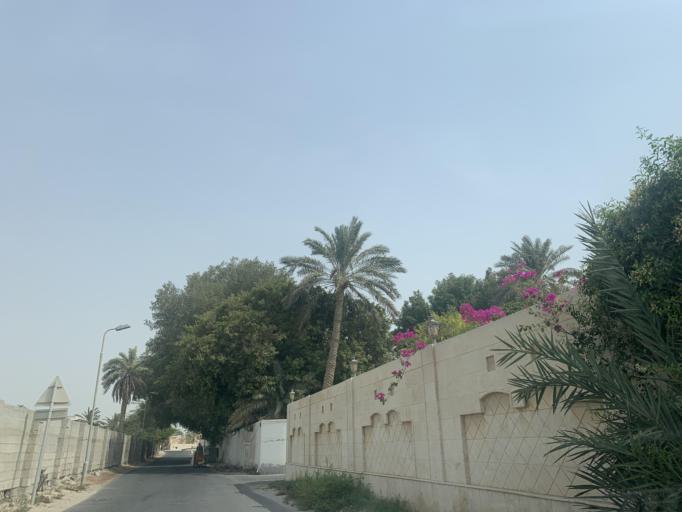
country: BH
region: Manama
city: Jidd Hafs
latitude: 26.1965
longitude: 50.4697
